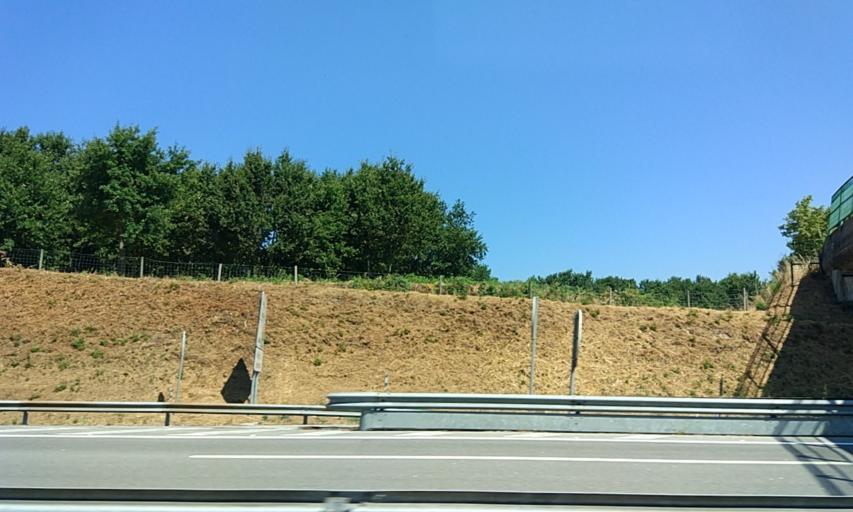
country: PT
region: Porto
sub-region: Lousada
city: Meinedo
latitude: 41.2313
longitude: -8.2079
